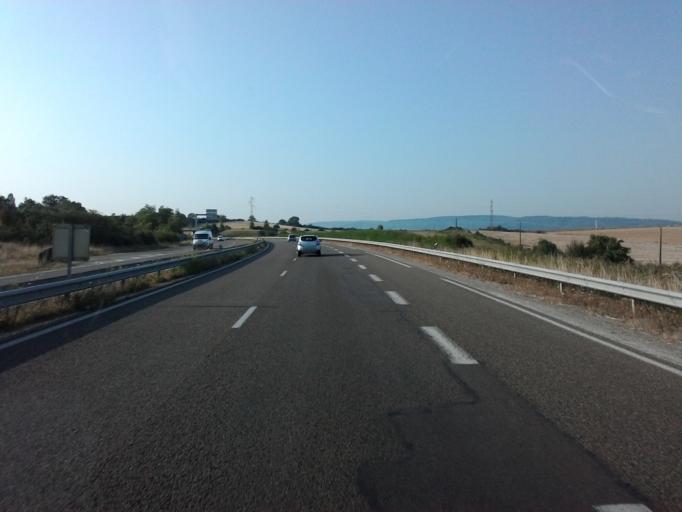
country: FR
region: Franche-Comte
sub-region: Departement de la Haute-Saone
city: Pusey
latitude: 47.6553
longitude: 6.1131
